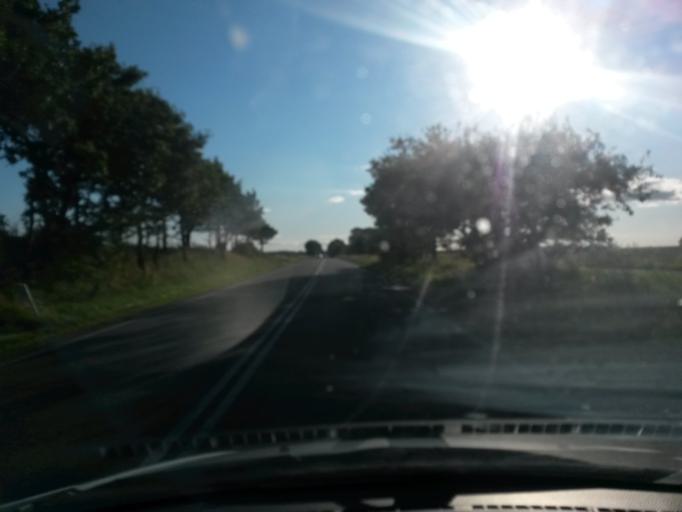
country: DK
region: Central Jutland
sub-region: Silkeborg Kommune
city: Kjellerup
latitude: 56.3022
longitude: 9.4610
